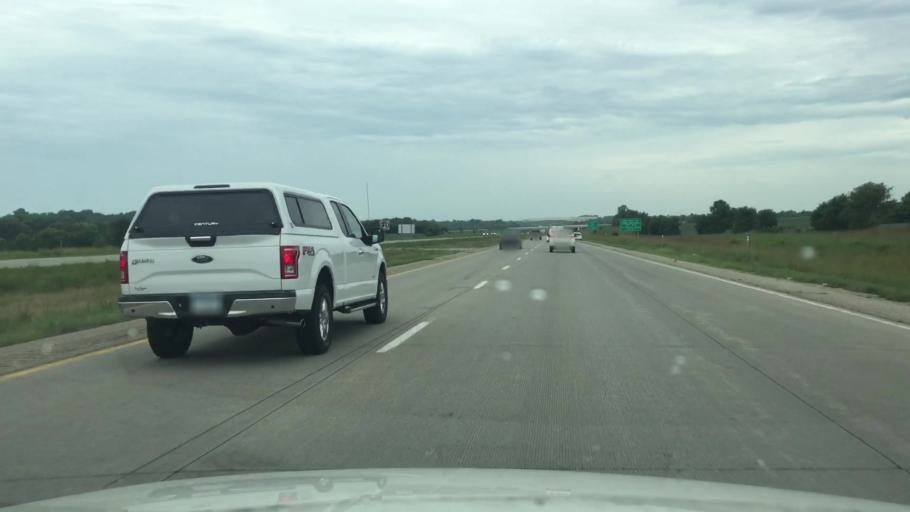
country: US
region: Iowa
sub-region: Warren County
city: Norwalk
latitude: 41.5019
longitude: -93.6325
